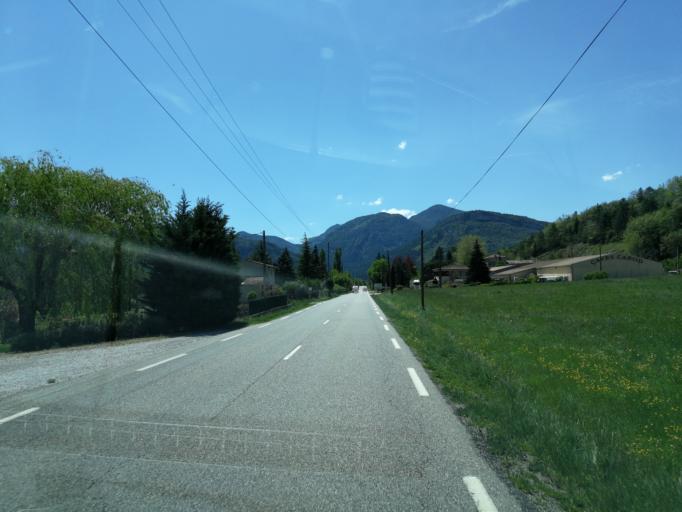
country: FR
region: Rhone-Alpes
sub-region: Departement de la Drome
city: Die
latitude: 44.7163
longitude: 5.2644
